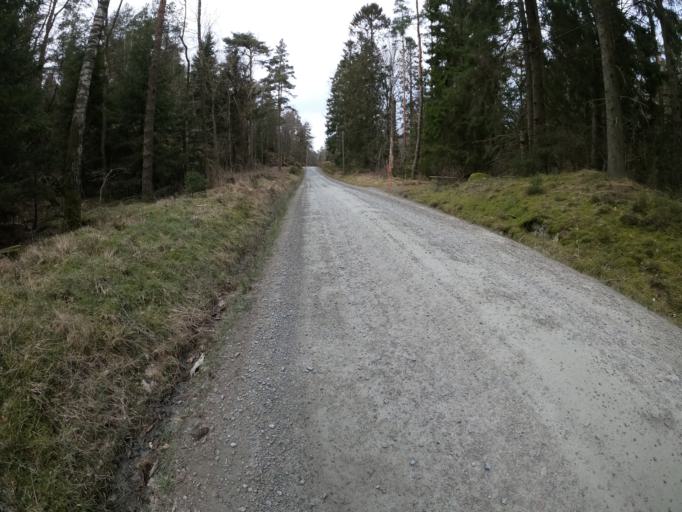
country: SE
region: Vaestra Goetaland
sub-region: Harryda Kommun
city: Molnlycke
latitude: 57.6369
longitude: 12.1007
